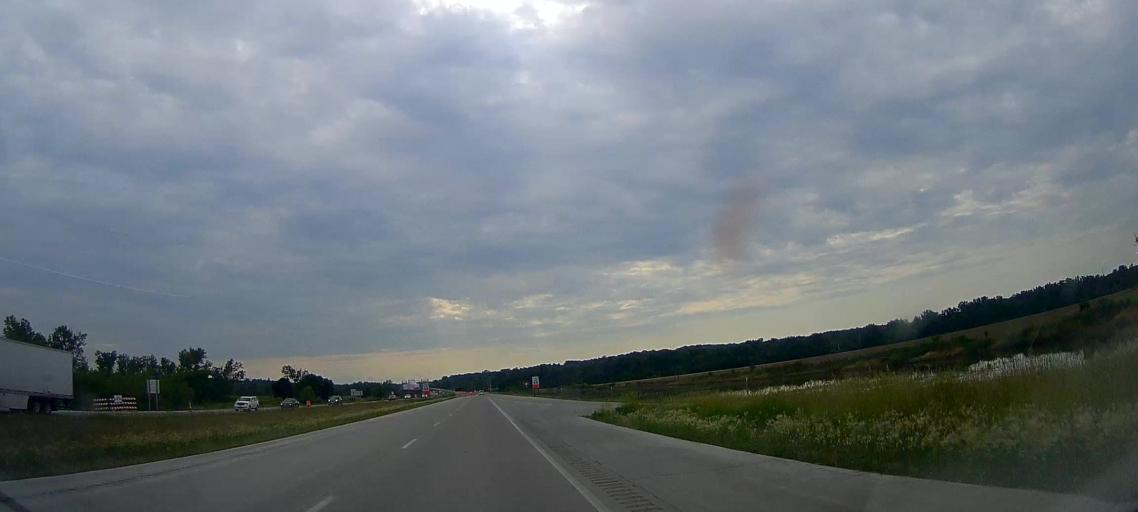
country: US
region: Iowa
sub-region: Pottawattamie County
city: Carter Lake
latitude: 41.3467
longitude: -95.9407
